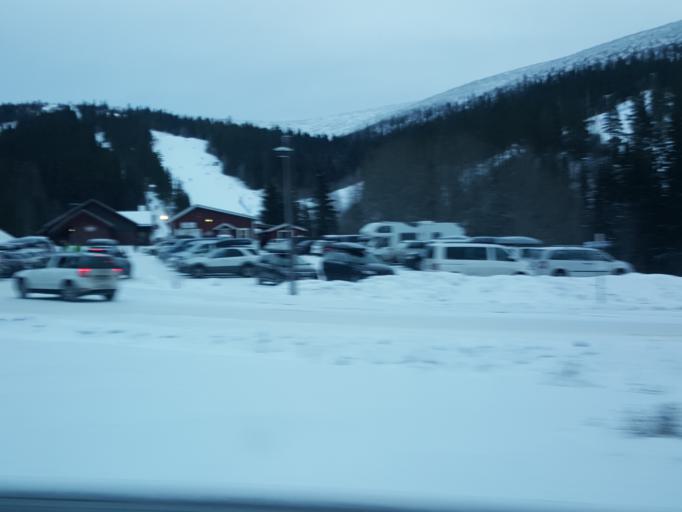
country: SE
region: Jaemtland
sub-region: Harjedalens Kommun
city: Sveg
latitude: 62.4209
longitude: 13.9541
